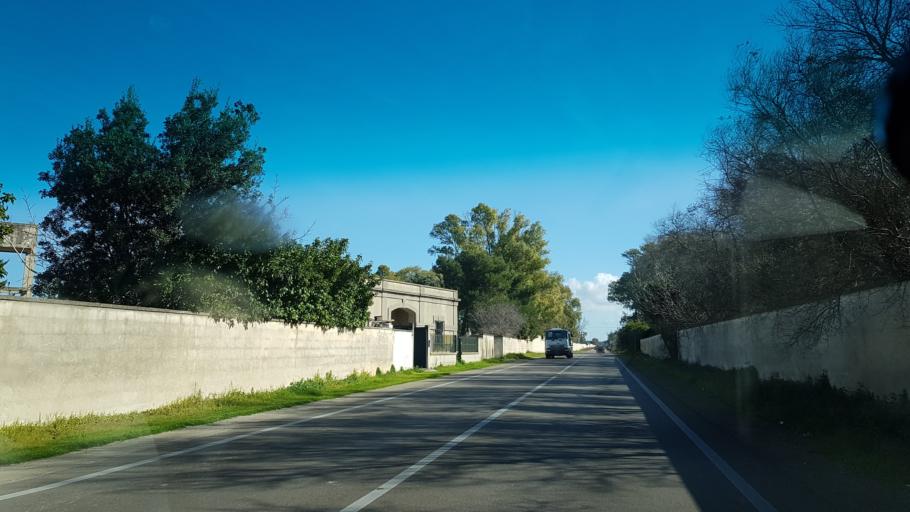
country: IT
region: Apulia
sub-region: Provincia di Lecce
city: Arnesano
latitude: 40.3593
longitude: 18.1110
